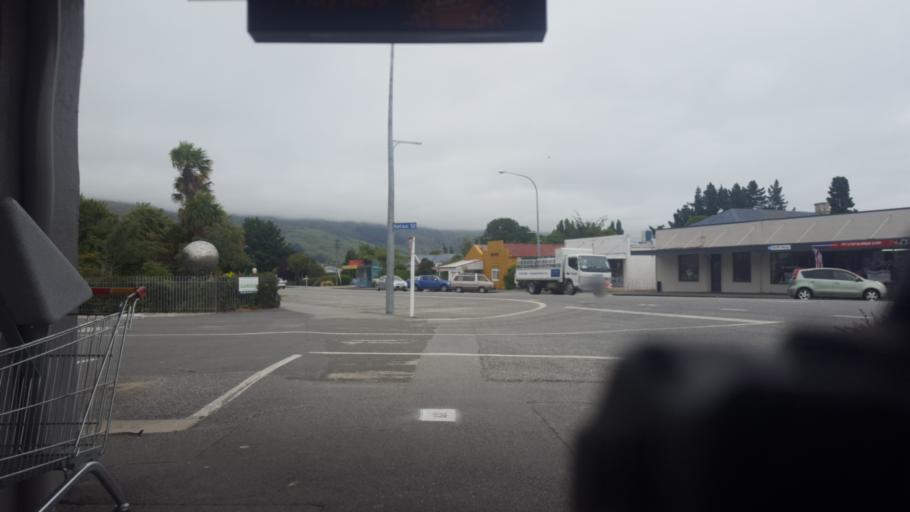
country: NZ
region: Otago
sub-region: Queenstown-Lakes District
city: Kingston
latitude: -45.5401
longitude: 169.3140
